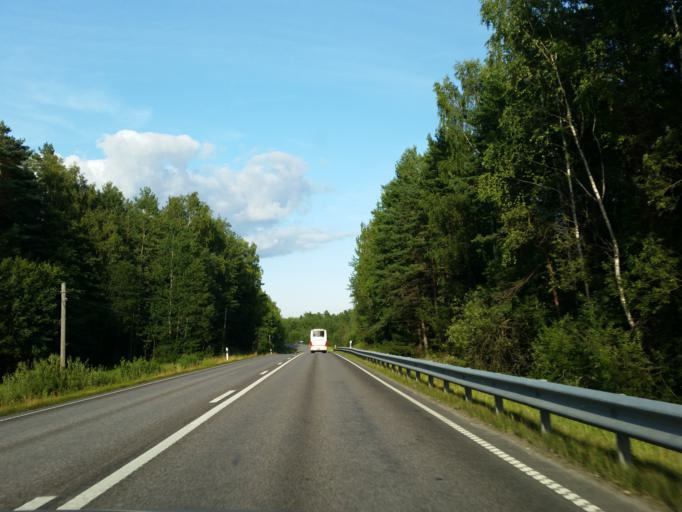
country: SE
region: Stockholm
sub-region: Sodertalje Kommun
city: Molnbo
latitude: 59.0601
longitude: 17.4872
